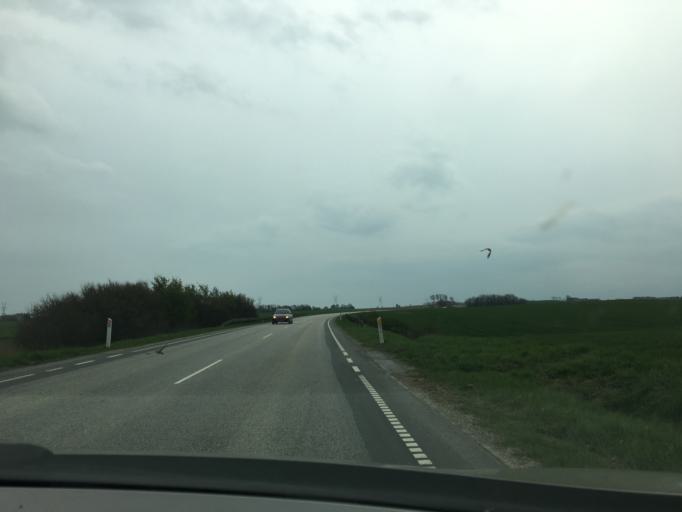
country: DK
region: Central Jutland
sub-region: Hedensted Kommune
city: Torring
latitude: 55.8158
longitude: 9.5790
